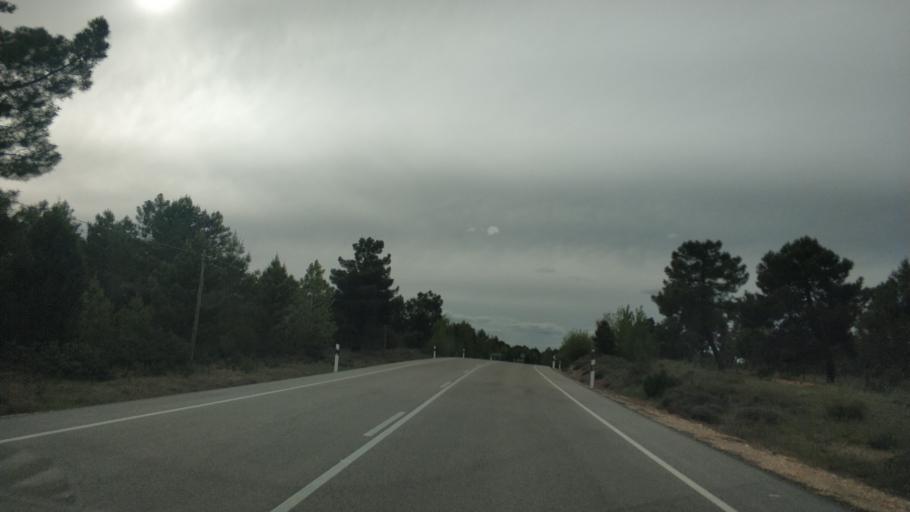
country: ES
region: Castille and Leon
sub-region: Provincia de Soria
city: Quintanas de Gormaz
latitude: 41.5305
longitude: -2.9468
